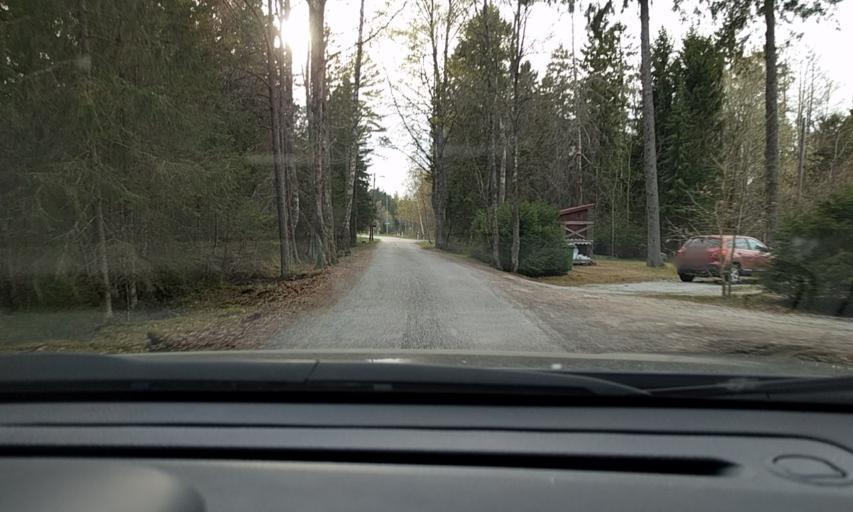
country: EE
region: Harju
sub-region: Viimsi vald
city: Viimsi
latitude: 59.5217
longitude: 24.8970
